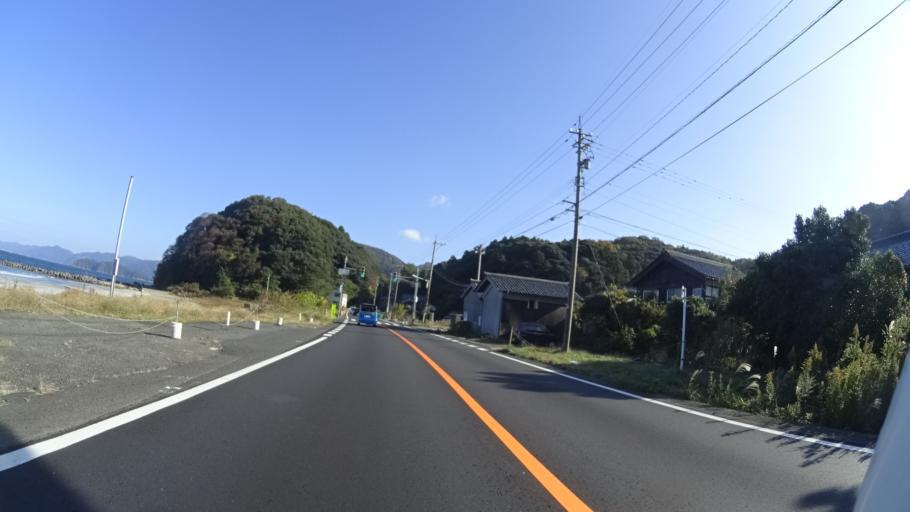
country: JP
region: Fukui
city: Tsuruga
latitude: 35.7047
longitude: 136.0830
